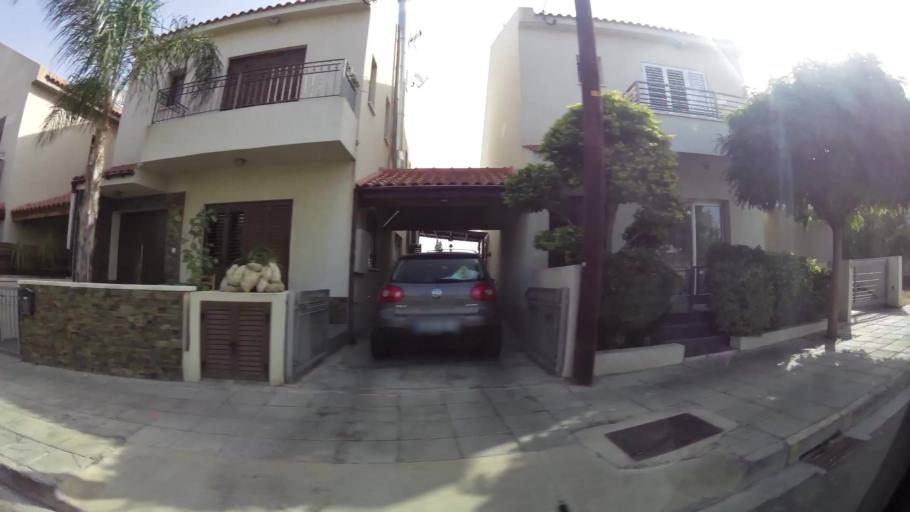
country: CY
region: Lefkosia
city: Geri
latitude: 35.0645
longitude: 33.3955
